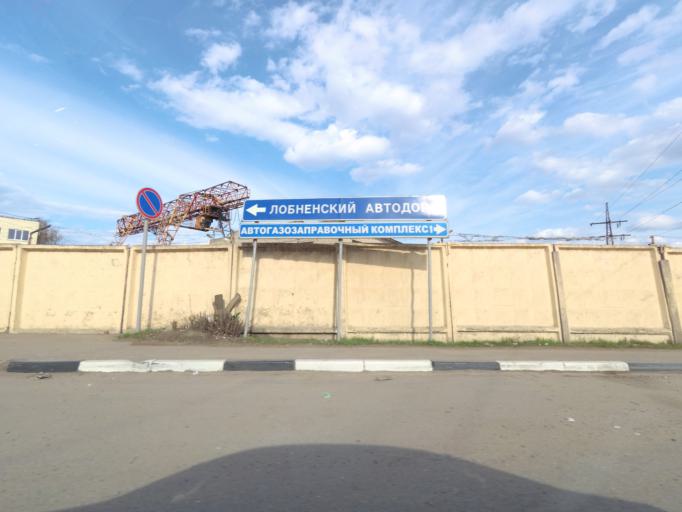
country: RU
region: Moskovskaya
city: Lobnya
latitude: 56.0141
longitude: 37.4373
